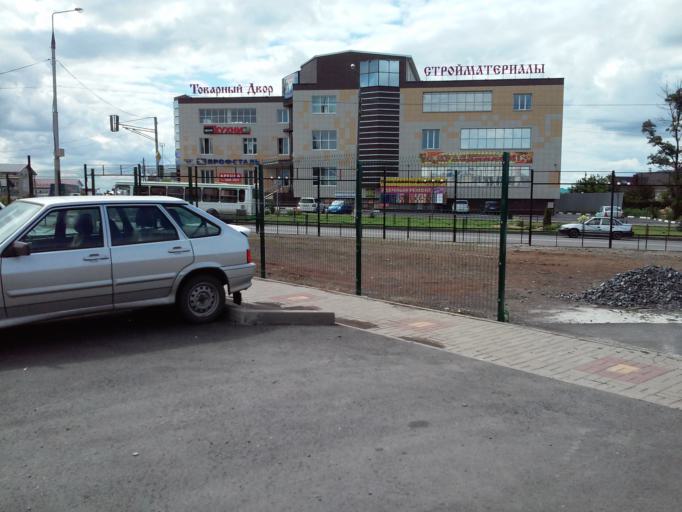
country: RU
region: Belgorod
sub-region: Belgorodskiy Rayon
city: Belgorod
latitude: 50.5338
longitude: 36.5749
